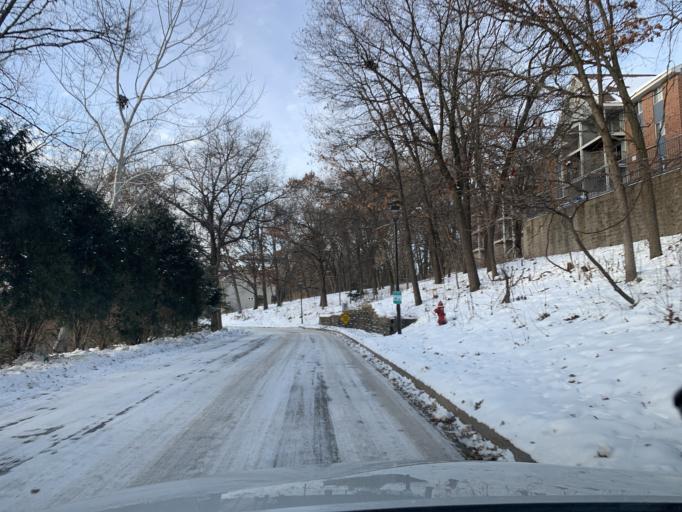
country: US
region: Minnesota
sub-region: Hennepin County
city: Minnetonka Mills
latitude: 44.9518
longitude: -93.4032
